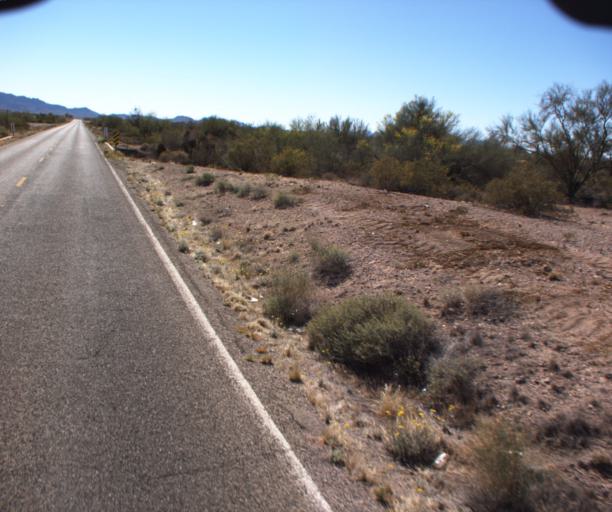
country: US
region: Arizona
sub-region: Pima County
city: Ajo
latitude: 32.3558
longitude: -112.8267
